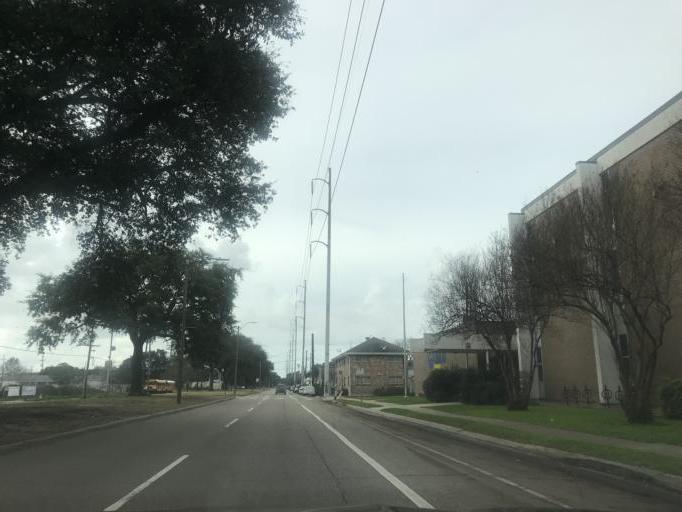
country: US
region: Louisiana
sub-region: Orleans Parish
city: New Orleans
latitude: 29.9472
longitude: -90.0897
